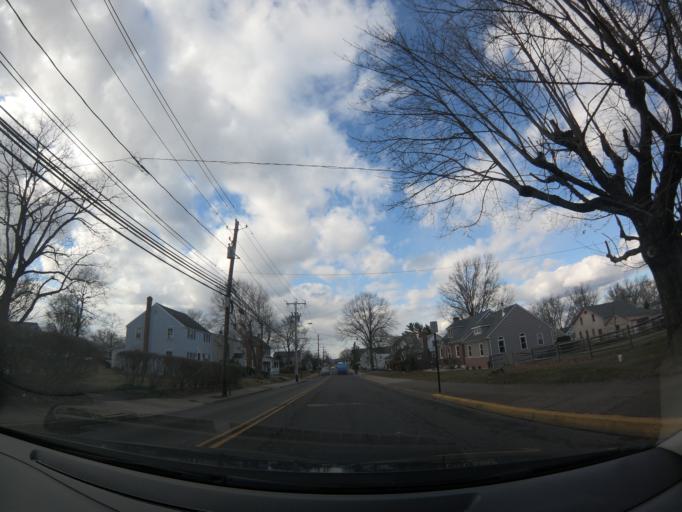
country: US
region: Pennsylvania
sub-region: Montgomery County
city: Telford
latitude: 40.3218
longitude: -75.3225
